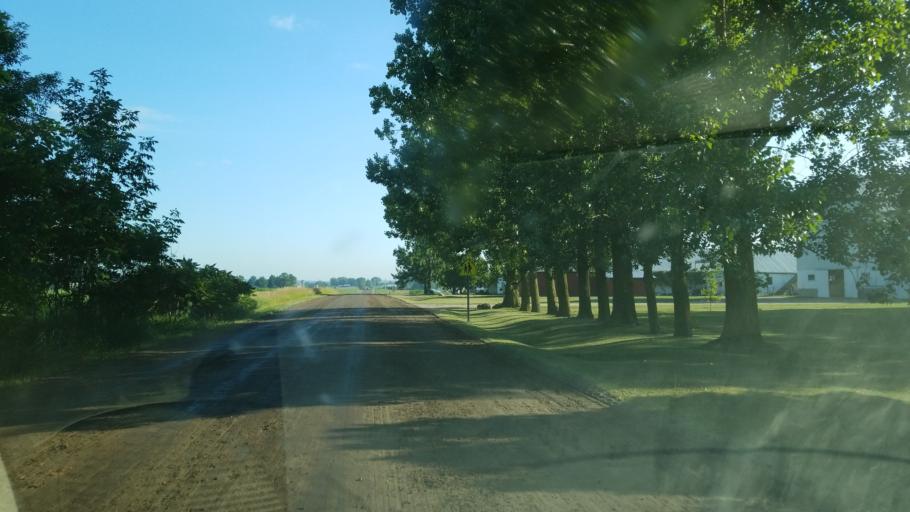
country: US
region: Michigan
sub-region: Mecosta County
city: Canadian Lakes
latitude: 43.5632
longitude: -85.3635
